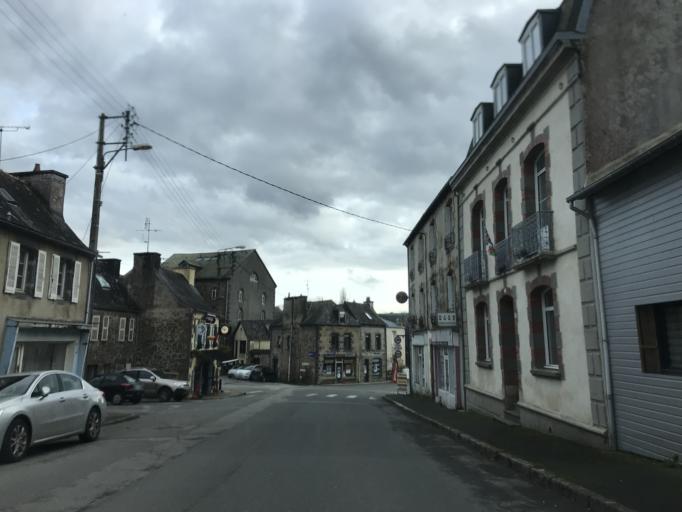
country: FR
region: Brittany
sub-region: Departement du Finistere
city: Le Faou
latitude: 48.2975
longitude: -4.1814
